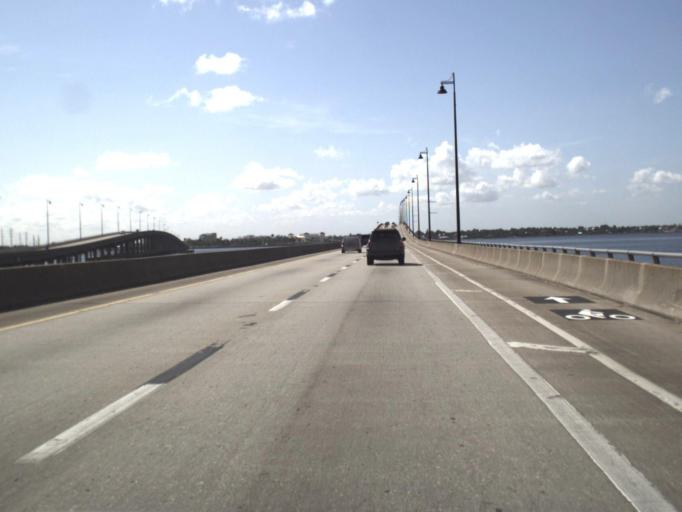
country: US
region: Florida
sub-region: Charlotte County
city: Charlotte Harbor
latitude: 26.9505
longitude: -82.0611
